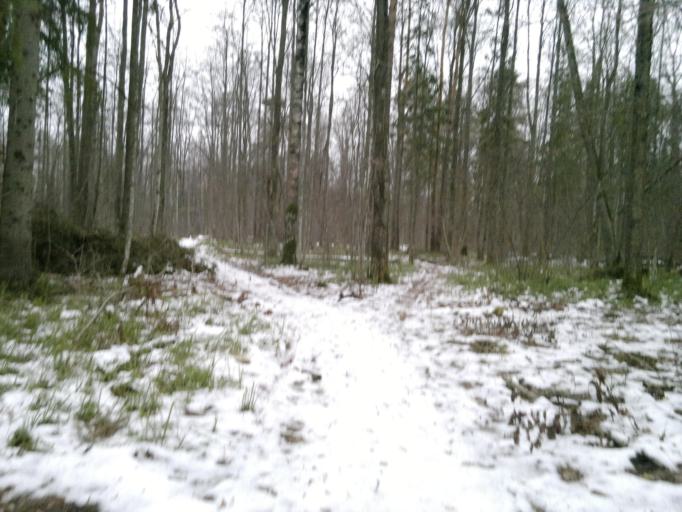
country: RU
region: Mariy-El
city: Yoshkar-Ola
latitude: 56.6129
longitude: 47.9464
